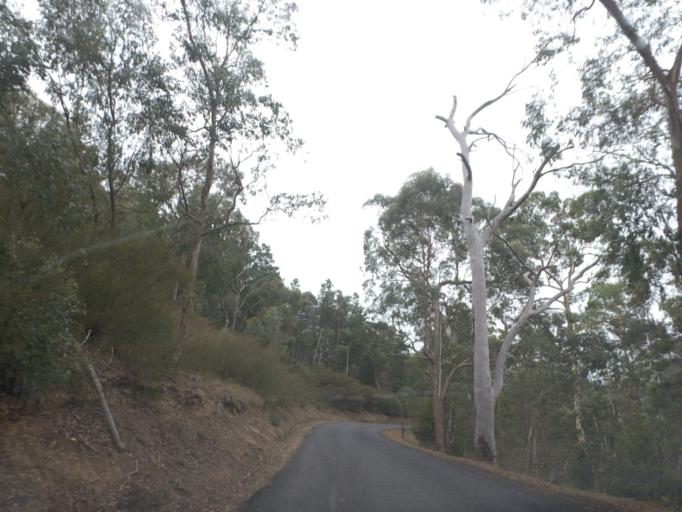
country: AU
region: Victoria
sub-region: Nillumbik
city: Saint Andrews
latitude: -37.5990
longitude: 145.2866
